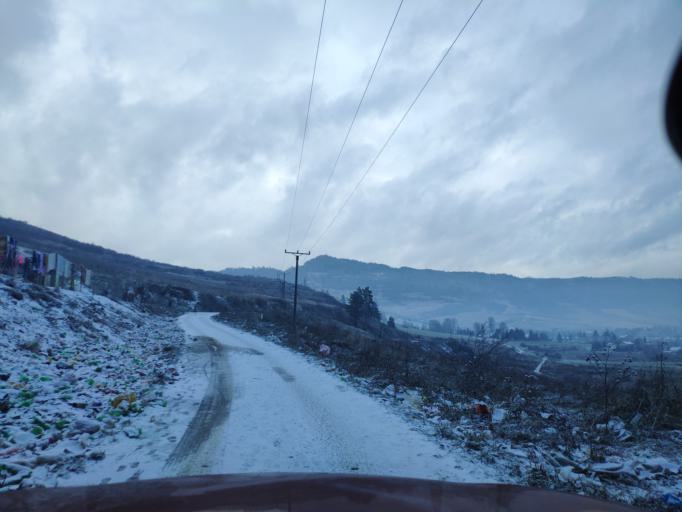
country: SK
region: Kosicky
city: Spisska Nova Ves
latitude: 48.8369
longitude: 20.6062
